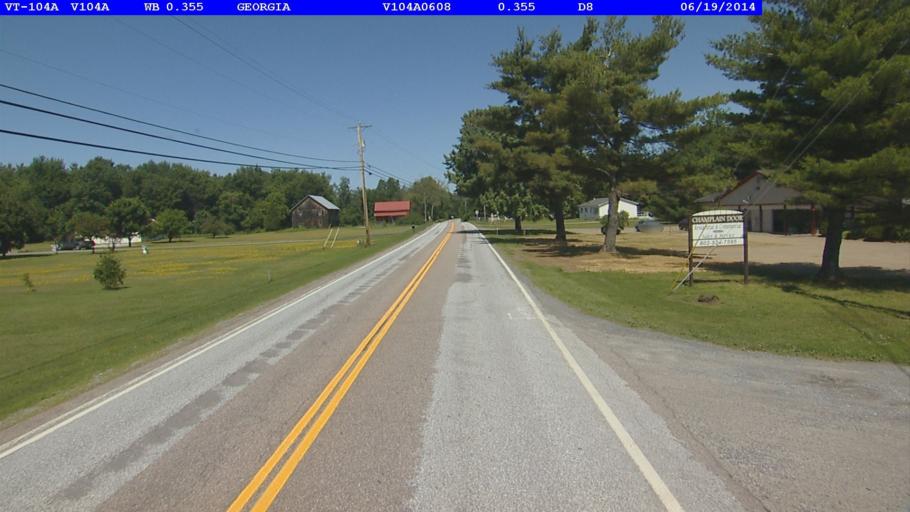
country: US
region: Vermont
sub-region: Chittenden County
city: Milton
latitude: 44.6915
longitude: -73.1025
